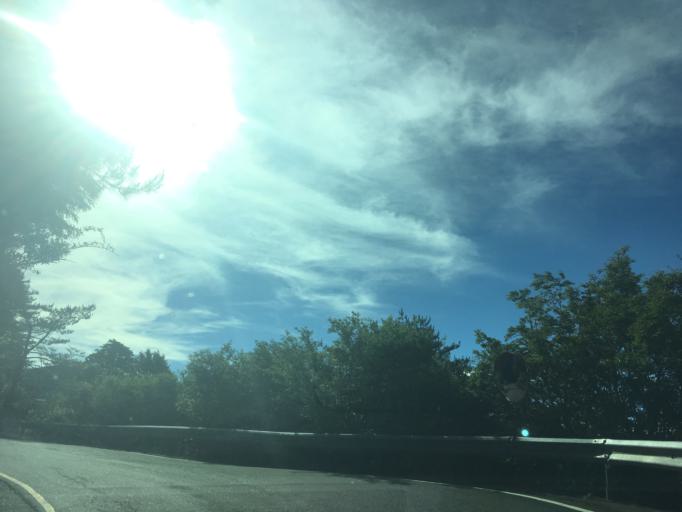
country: TW
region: Taiwan
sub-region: Nantou
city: Puli
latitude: 24.1173
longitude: 121.2346
